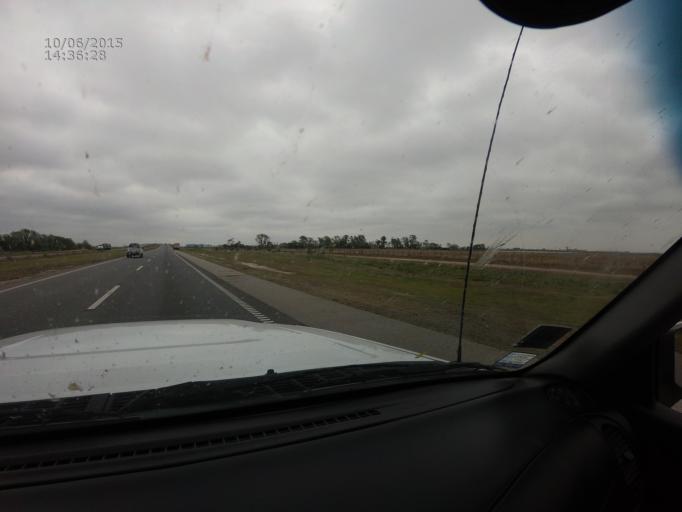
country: AR
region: Cordoba
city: James Craik
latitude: -32.1225
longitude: -63.4474
